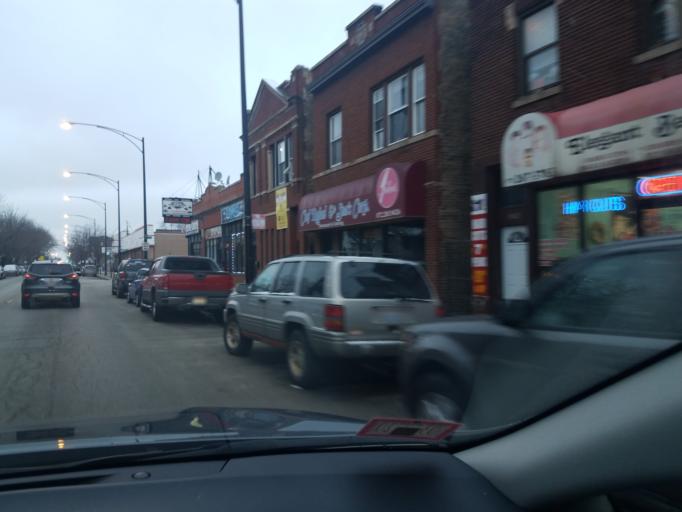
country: US
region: Illinois
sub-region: Cook County
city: Lincolnwood
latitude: 41.9610
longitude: -87.7235
